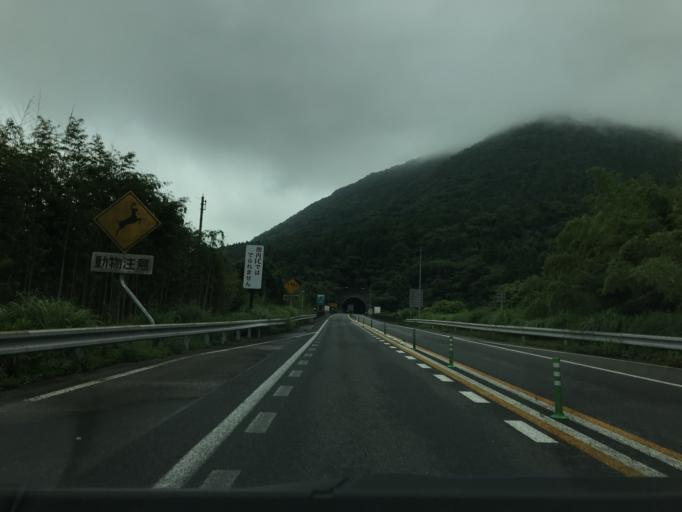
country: JP
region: Oita
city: Bungo-Takada-shi
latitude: 33.4904
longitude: 131.3230
